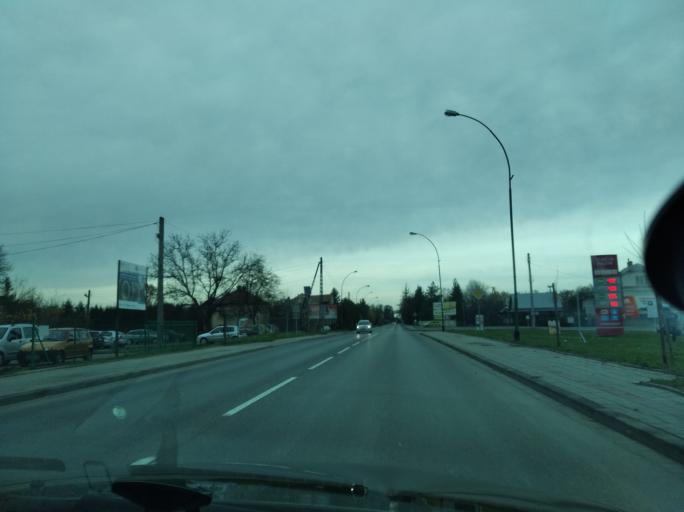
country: PL
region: Subcarpathian Voivodeship
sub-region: Powiat lancucki
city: Lancut
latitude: 50.0914
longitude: 22.2316
